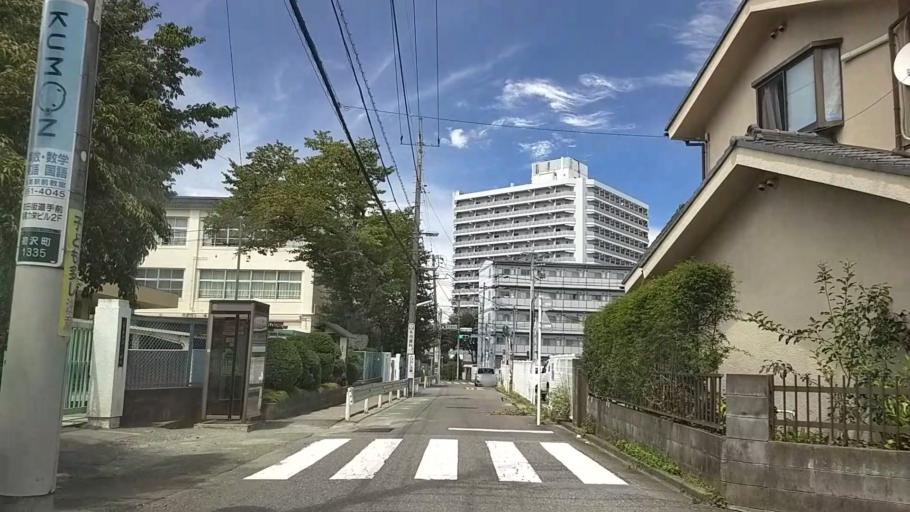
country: JP
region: Tokyo
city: Hachioji
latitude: 35.6402
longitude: 139.2827
